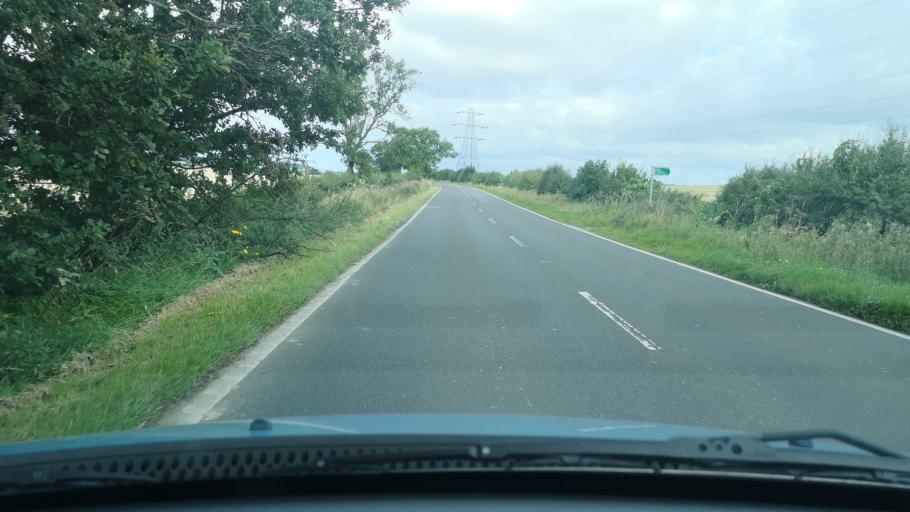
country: GB
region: England
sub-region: Barnsley
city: Royston
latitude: 53.6178
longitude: -1.4412
